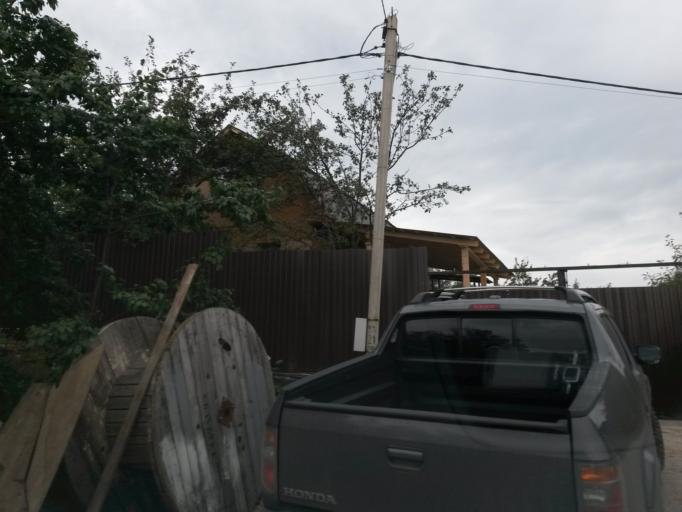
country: RU
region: Moskovskaya
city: Alekseyevka
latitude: 55.6079
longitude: 37.8078
